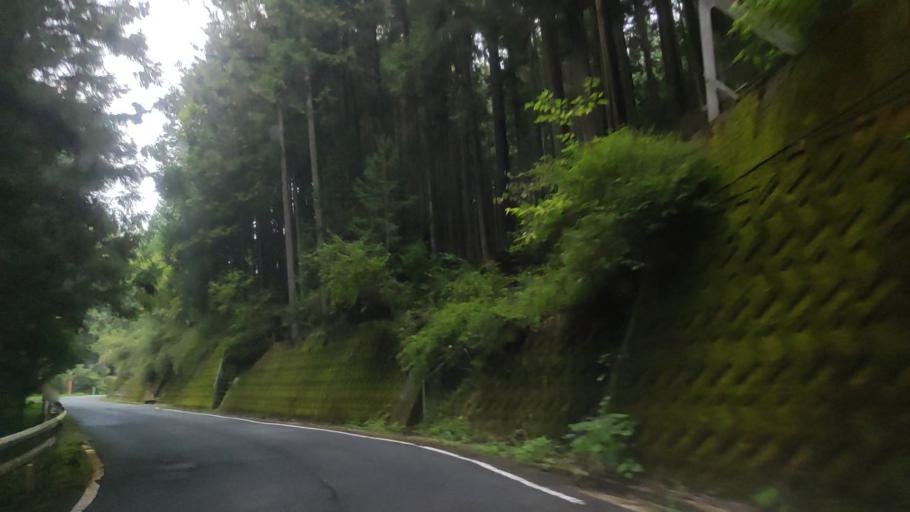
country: JP
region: Wakayama
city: Hashimoto
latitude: 34.2809
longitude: 135.6286
